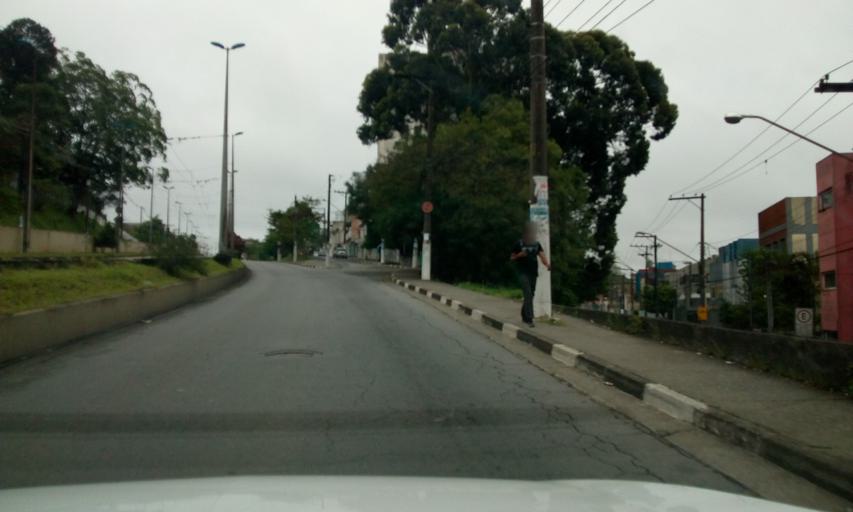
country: BR
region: Sao Paulo
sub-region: Diadema
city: Diadema
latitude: -23.6823
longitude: -46.6262
